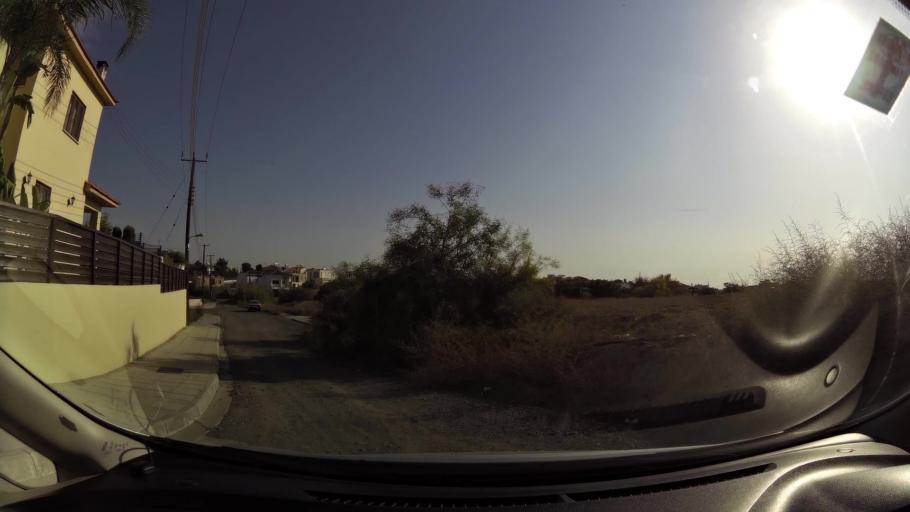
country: CY
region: Larnaka
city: Aradippou
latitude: 34.9497
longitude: 33.5988
